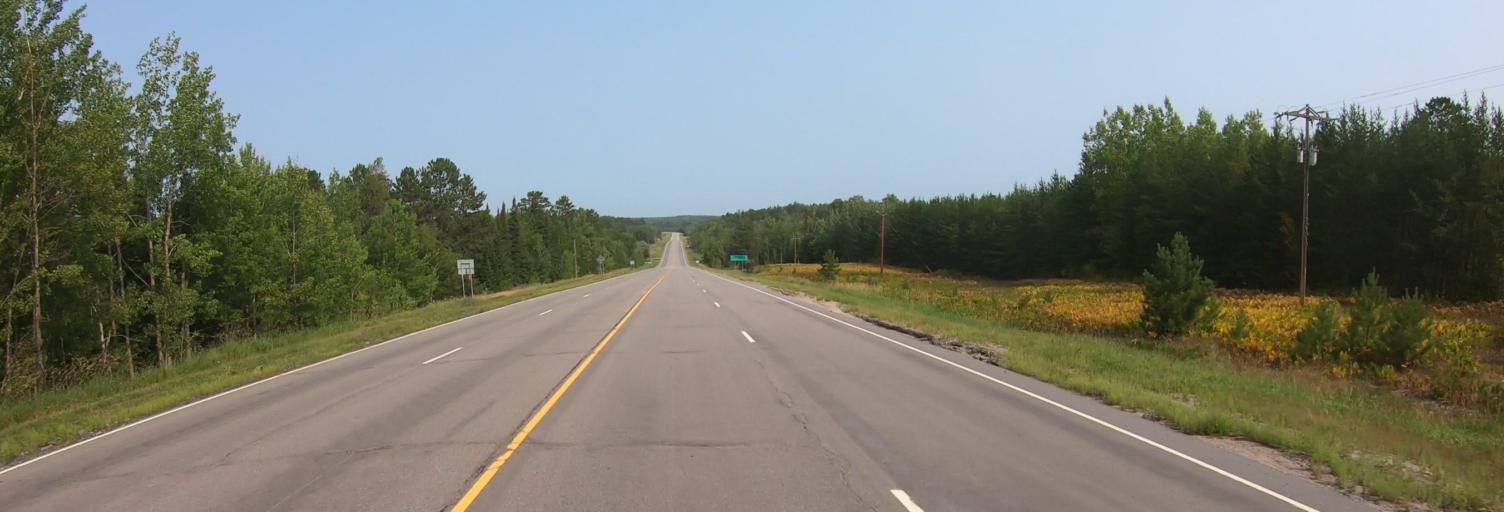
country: US
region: Minnesota
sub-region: Saint Louis County
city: Mountain Iron
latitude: 48.0685
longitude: -92.8226
